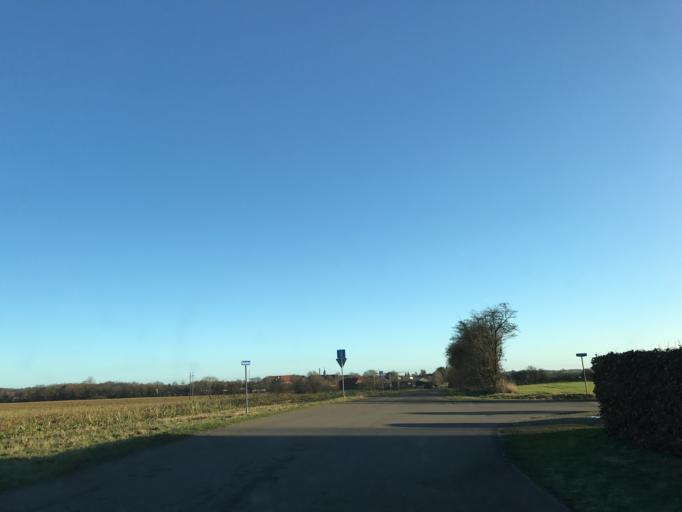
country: DK
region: South Denmark
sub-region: Kolding Kommune
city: Christiansfeld
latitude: 55.3593
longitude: 9.4689
